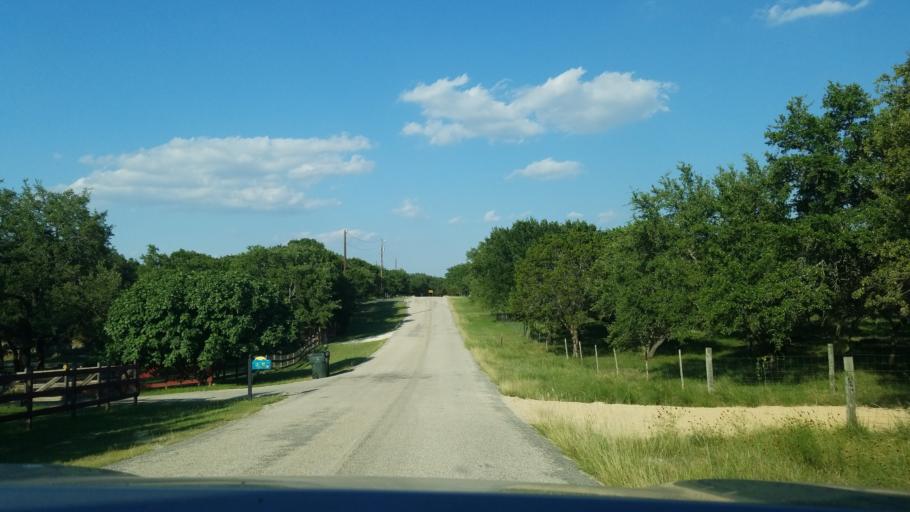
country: US
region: Texas
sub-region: Comal County
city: Bulverde
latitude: 29.7798
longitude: -98.4436
